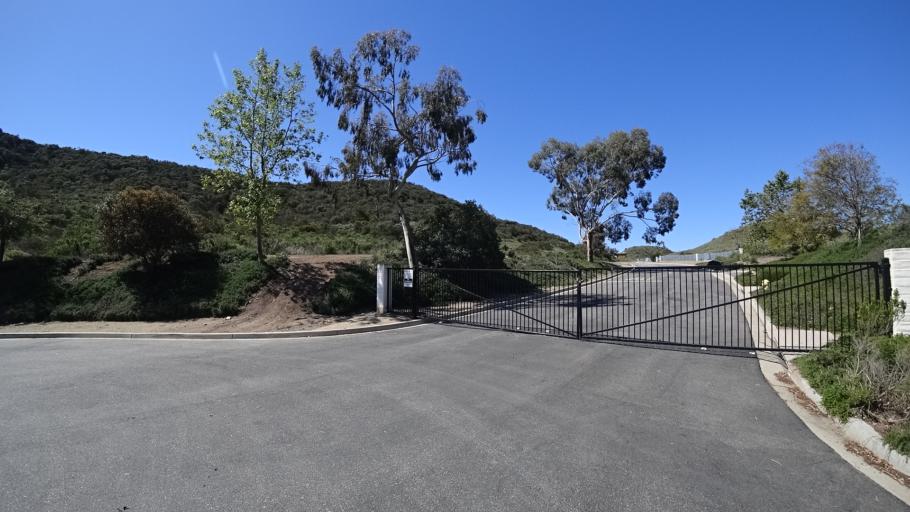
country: US
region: California
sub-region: Ventura County
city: Casa Conejo
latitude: 34.1648
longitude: -118.9783
